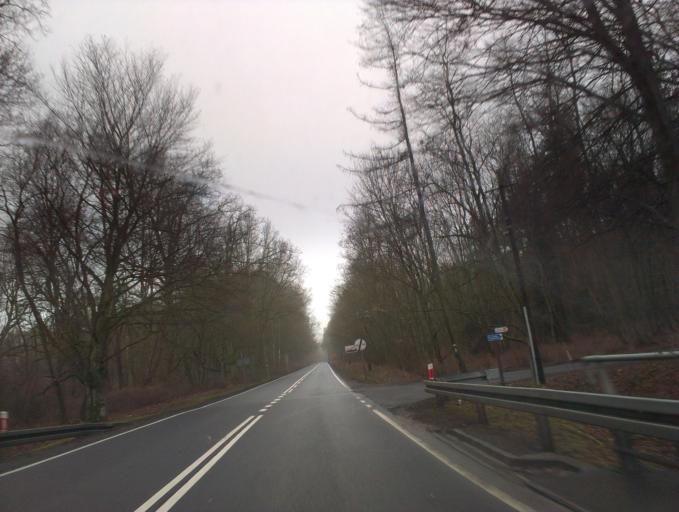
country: PL
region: Greater Poland Voivodeship
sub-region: Powiat zlotowski
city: Tarnowka
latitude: 53.3041
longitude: 16.7929
